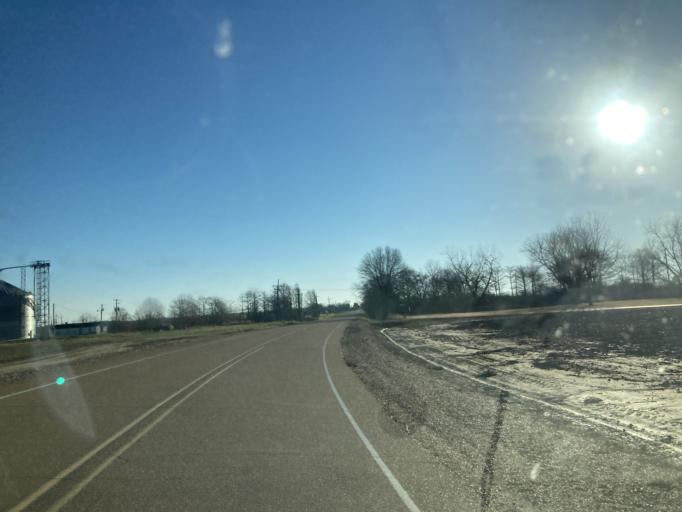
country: US
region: Mississippi
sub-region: Yazoo County
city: Yazoo City
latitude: 32.9310
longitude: -90.6012
